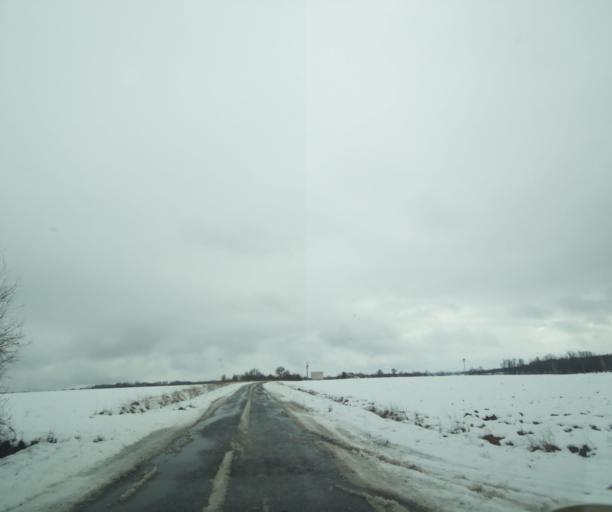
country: FR
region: Champagne-Ardenne
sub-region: Departement de la Haute-Marne
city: Montier-en-Der
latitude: 48.4189
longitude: 4.7319
